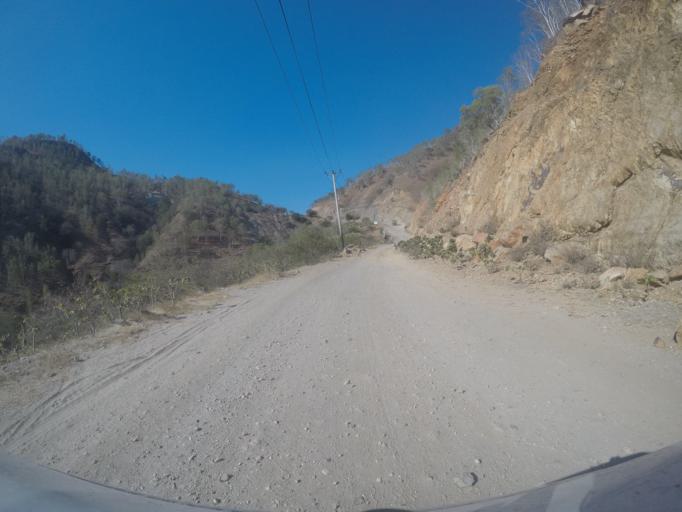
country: TL
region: Dili
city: Dili
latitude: -8.5323
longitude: 125.6184
